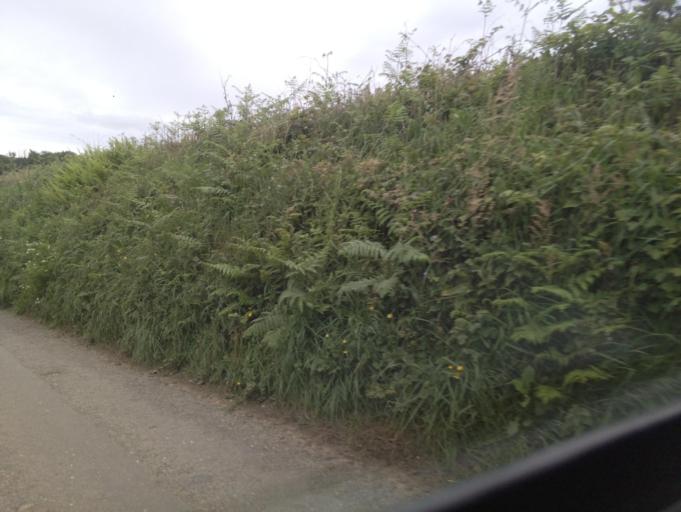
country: GB
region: England
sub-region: Devon
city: Dartmouth
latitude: 50.3348
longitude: -3.6482
